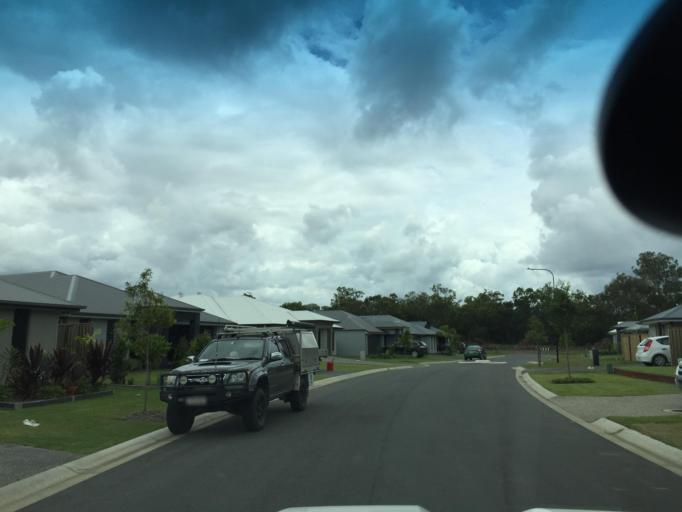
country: AU
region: Queensland
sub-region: Moreton Bay
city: Caboolture
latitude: -27.0607
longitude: 152.9250
